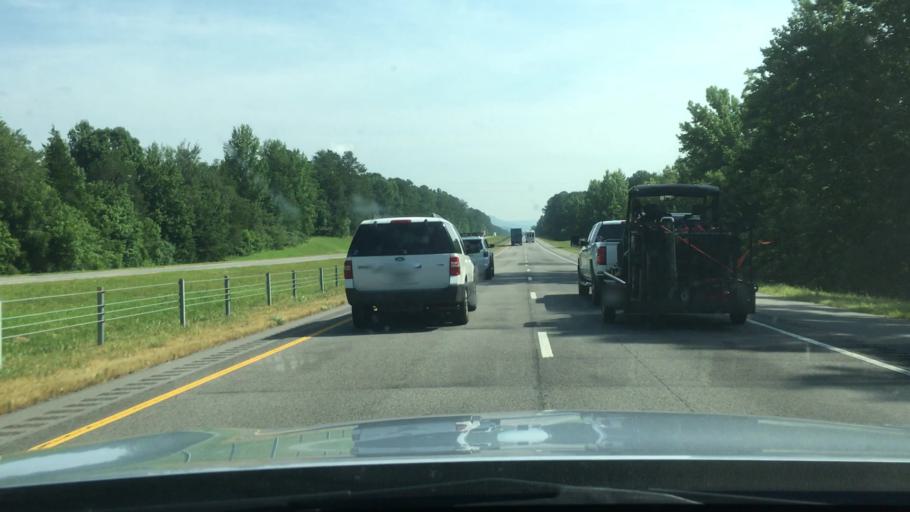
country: US
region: Alabama
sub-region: DeKalb County
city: Henagar
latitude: 34.6331
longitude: -85.6201
